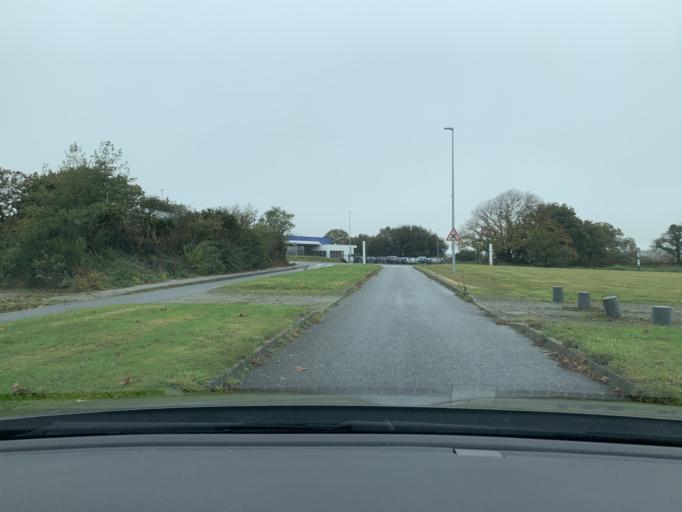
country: FR
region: Brittany
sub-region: Departement du Finistere
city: Roscanvel
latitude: 48.3600
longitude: -4.5683
